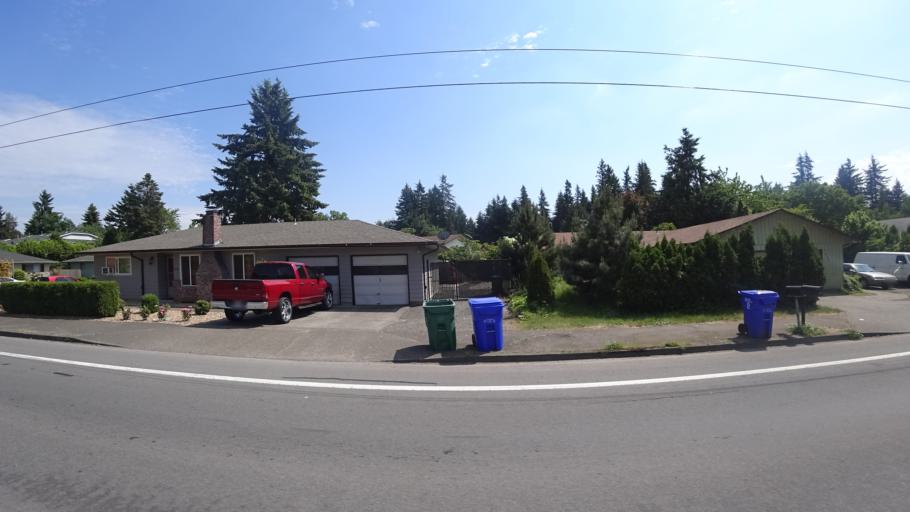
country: US
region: Oregon
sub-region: Multnomah County
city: Fairview
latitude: 45.5343
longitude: -122.4904
